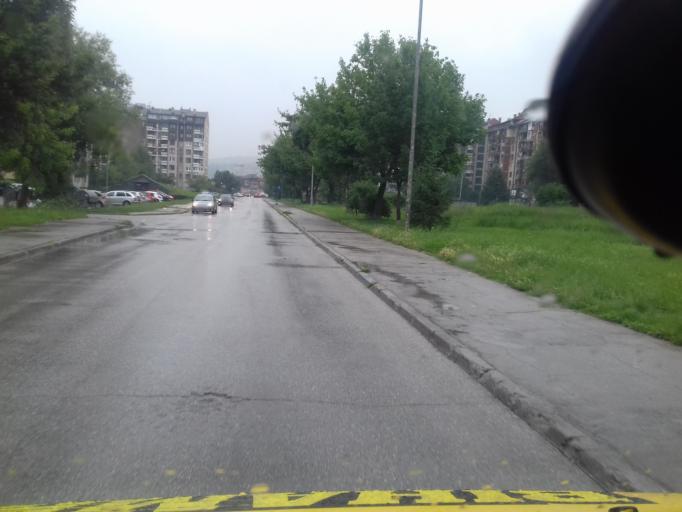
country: BA
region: Federation of Bosnia and Herzegovina
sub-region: Kanton Sarajevo
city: Sarajevo
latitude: 43.8387
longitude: 18.3400
